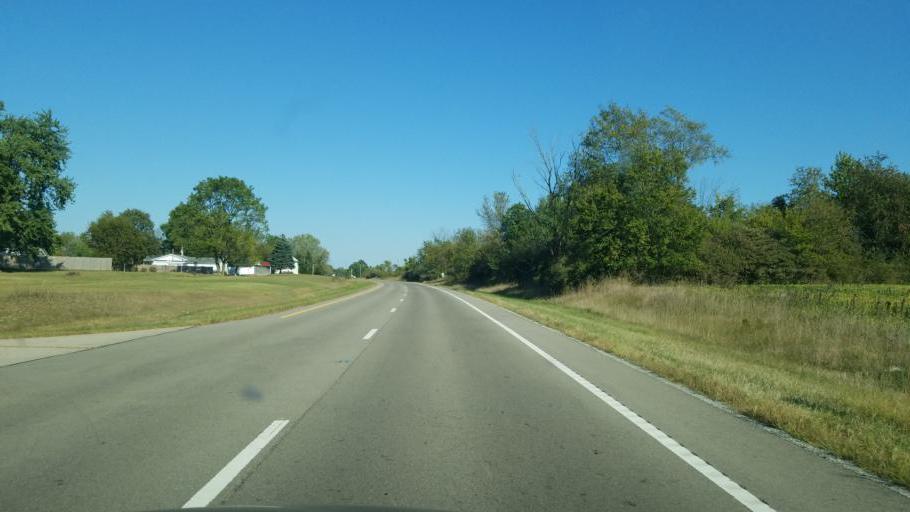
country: US
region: Ohio
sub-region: Madison County
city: Choctaw Lake
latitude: 39.9292
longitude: -83.5611
